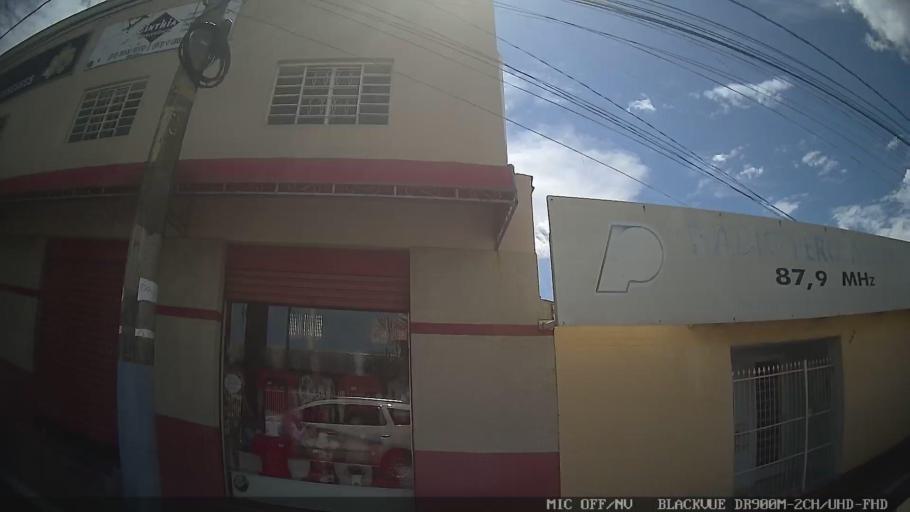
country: BR
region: Sao Paulo
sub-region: Conchas
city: Conchas
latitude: -23.0233
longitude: -48.0116
